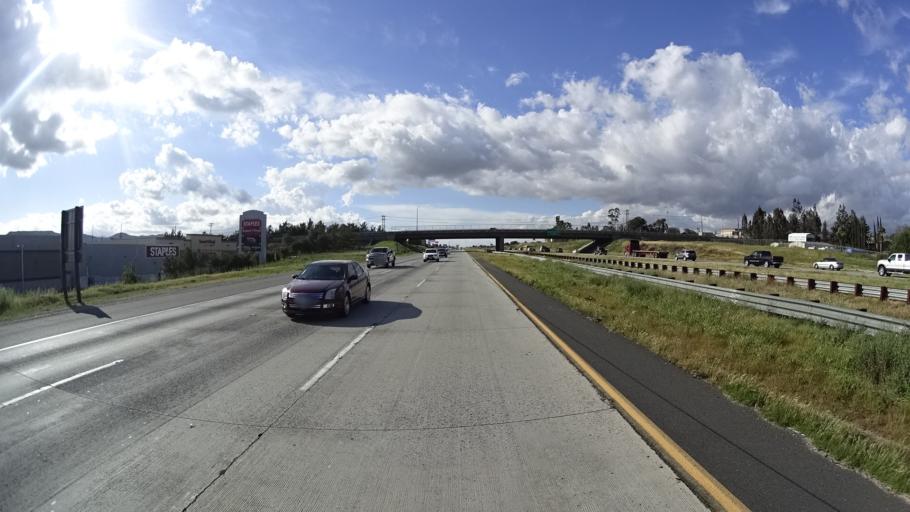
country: US
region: California
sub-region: Riverside County
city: Murrieta
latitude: 33.5588
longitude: -117.1985
